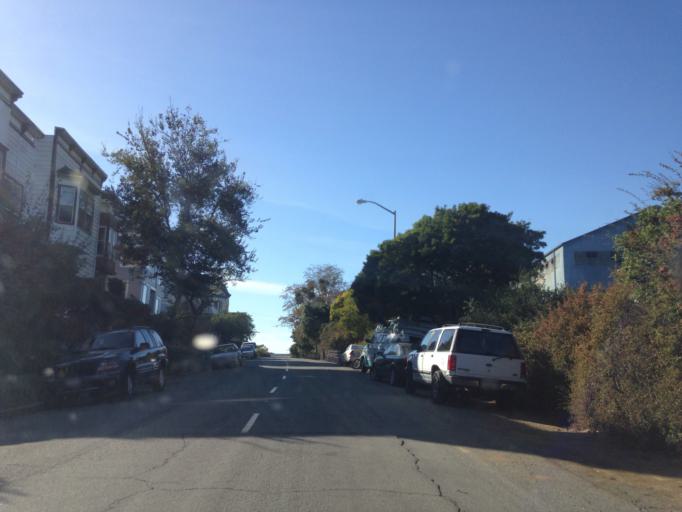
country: US
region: California
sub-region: Contra Costa County
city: Crockett
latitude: 38.0559
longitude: -122.2137
